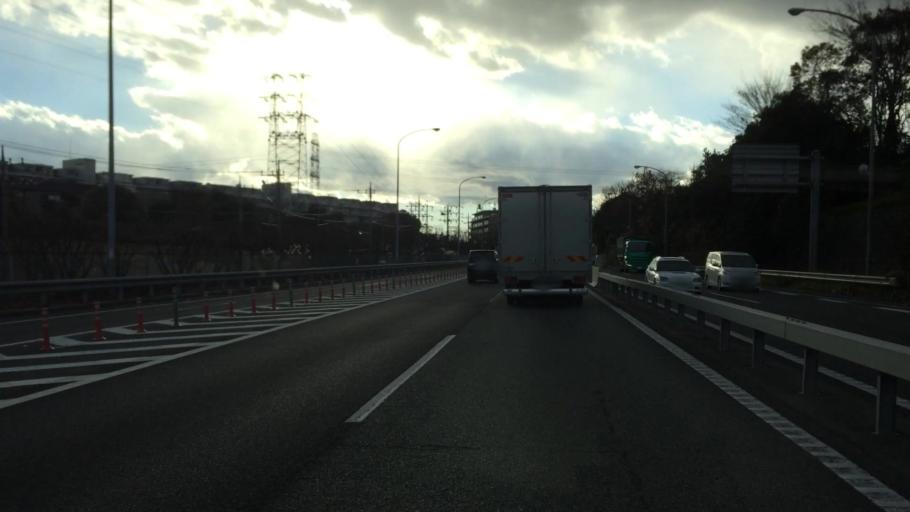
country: JP
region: Kanagawa
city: Yokohama
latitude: 35.4295
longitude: 139.5490
